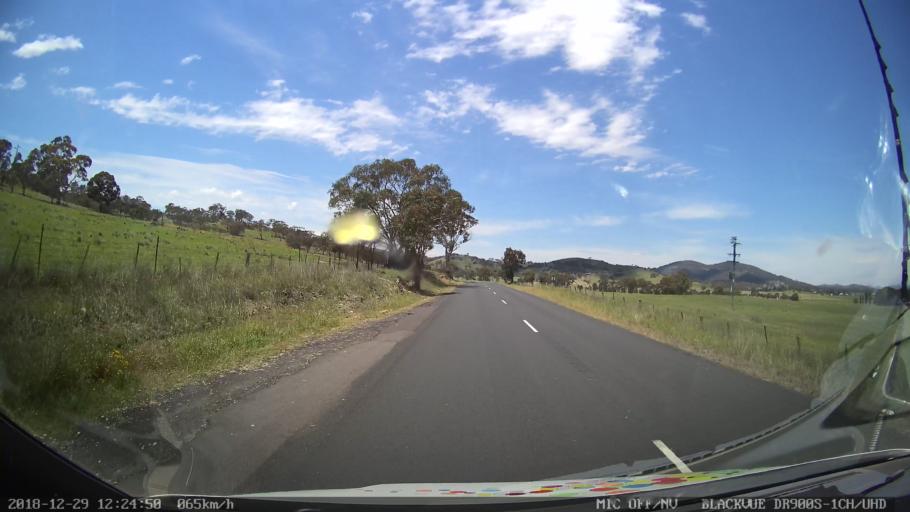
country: AU
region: Australian Capital Territory
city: Macarthur
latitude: -35.4504
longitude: 149.2101
